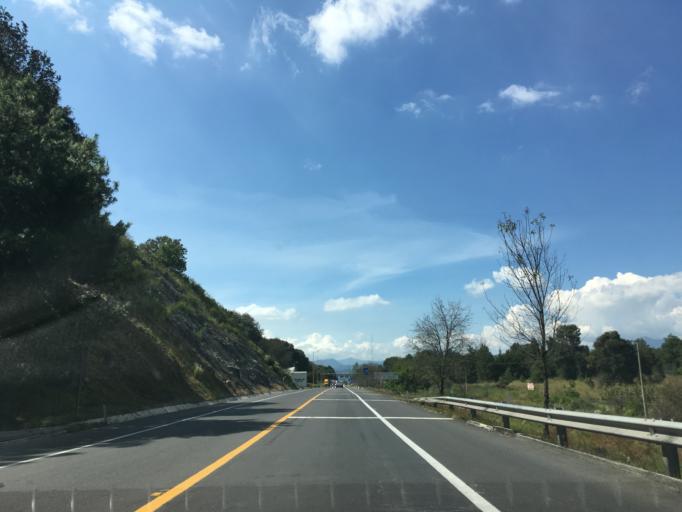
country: MX
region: Michoacan
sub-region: Patzcuaro
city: Santa Ana Chapitiro
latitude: 19.5047
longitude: -101.6549
